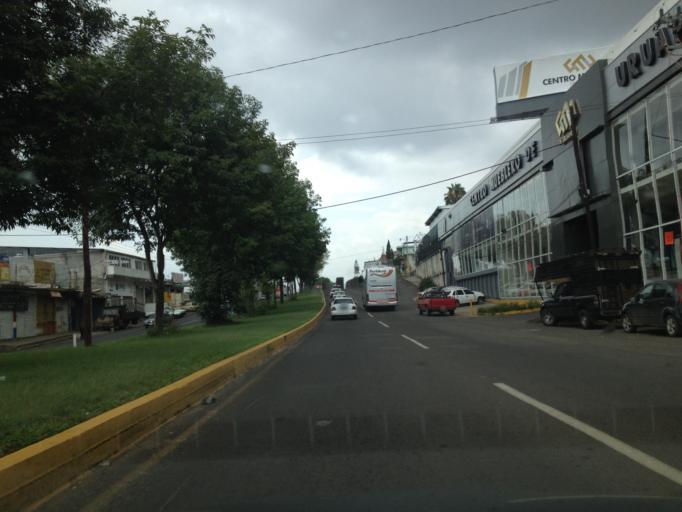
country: MX
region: Michoacan
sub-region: Uruapan
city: Uruapan
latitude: 19.4285
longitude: -102.0346
